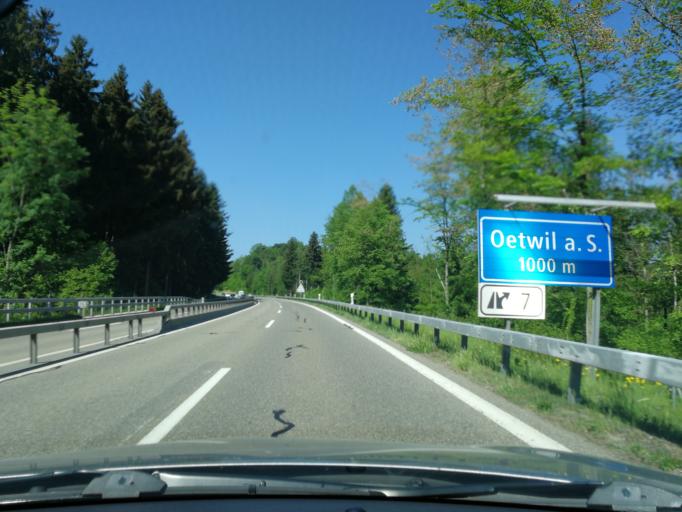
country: CH
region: Zurich
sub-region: Bezirk Hinwil
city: Binzikon
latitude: 47.2896
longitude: 8.7493
